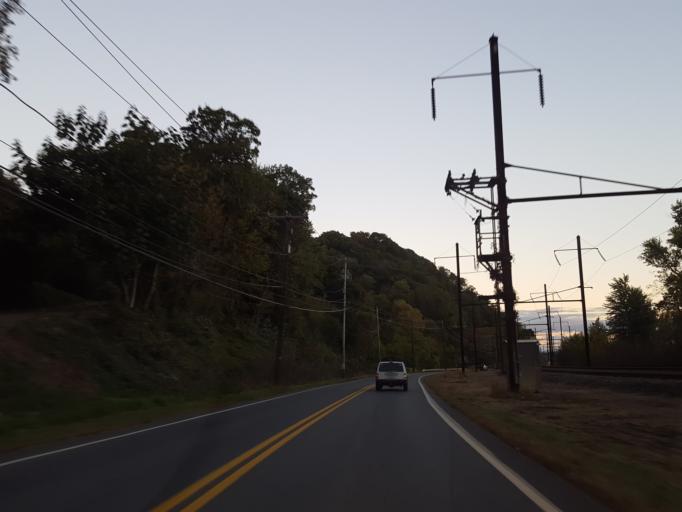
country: US
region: Pennsylvania
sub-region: Lancaster County
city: Columbia
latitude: 40.0234
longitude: -76.4930
